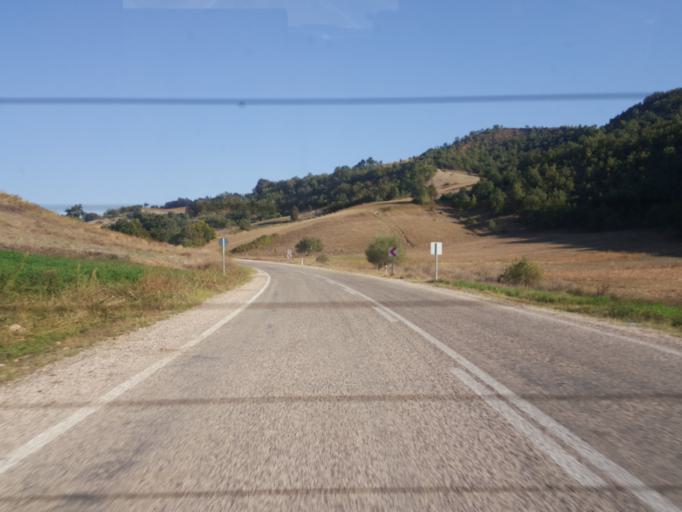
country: TR
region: Amasya
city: Tasova
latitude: 40.7194
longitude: 36.3047
